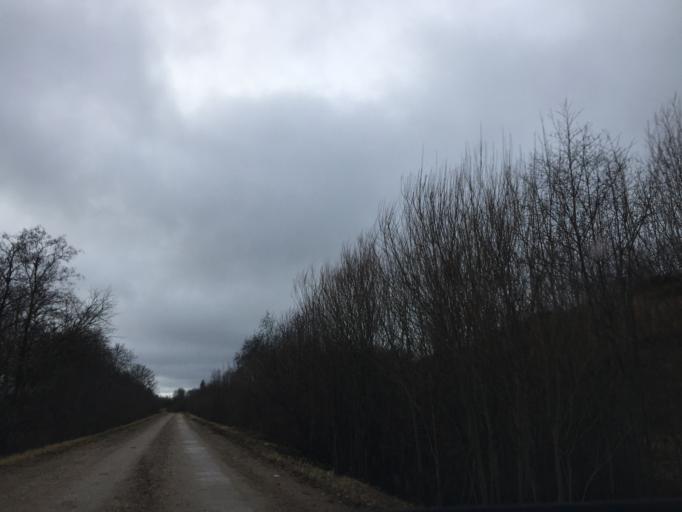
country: LV
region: Broceni
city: Broceni
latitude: 56.6698
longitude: 22.5553
